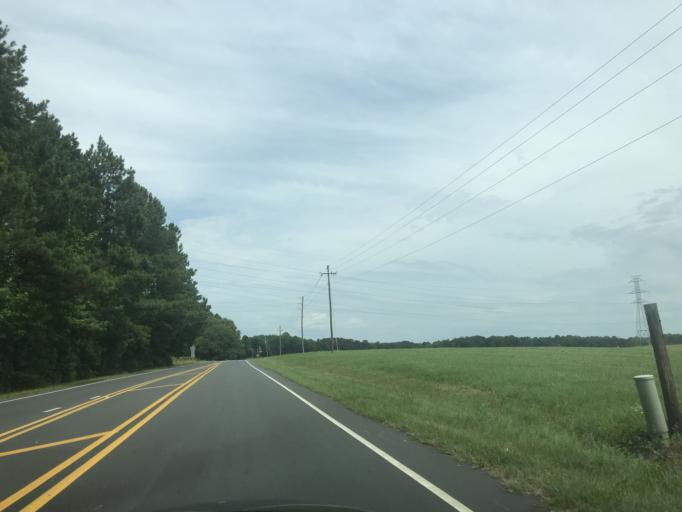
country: US
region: North Carolina
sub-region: Vance County
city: South Henderson
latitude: 36.2977
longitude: -78.4180
